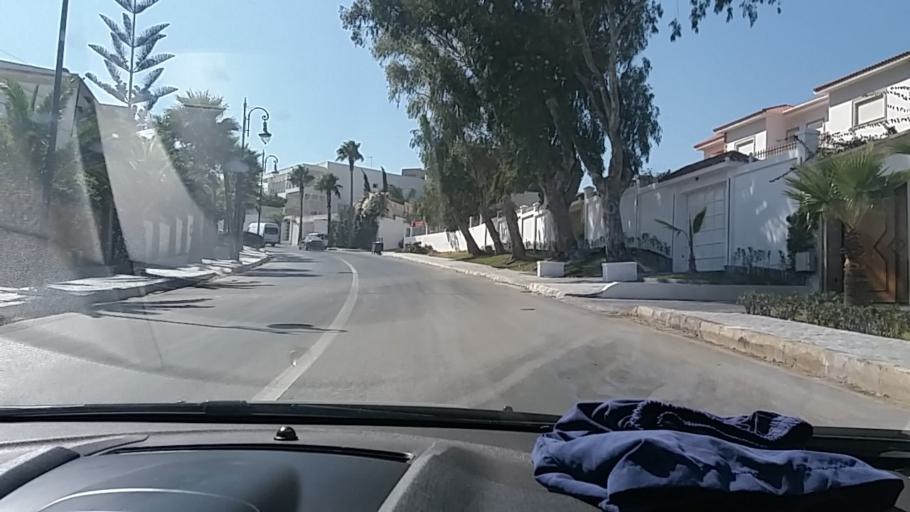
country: MA
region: Tanger-Tetouan
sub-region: Tanger-Assilah
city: Tangier
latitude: 35.7791
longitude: -5.8584
